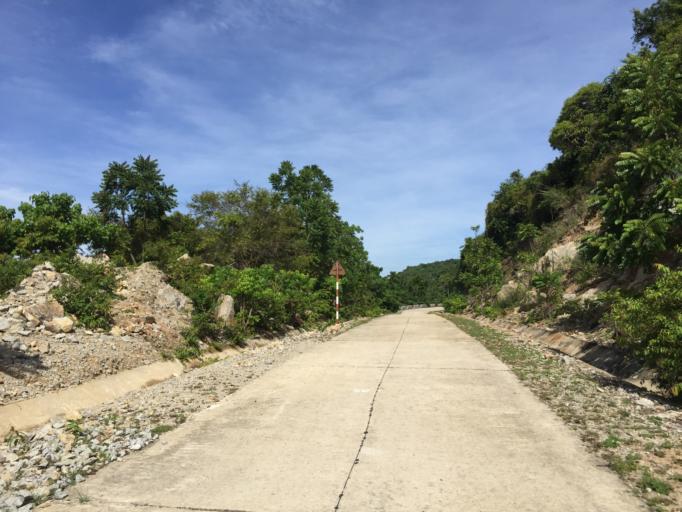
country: VN
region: Quang Nam
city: Hoi An
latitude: 15.9322
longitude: 108.5316
